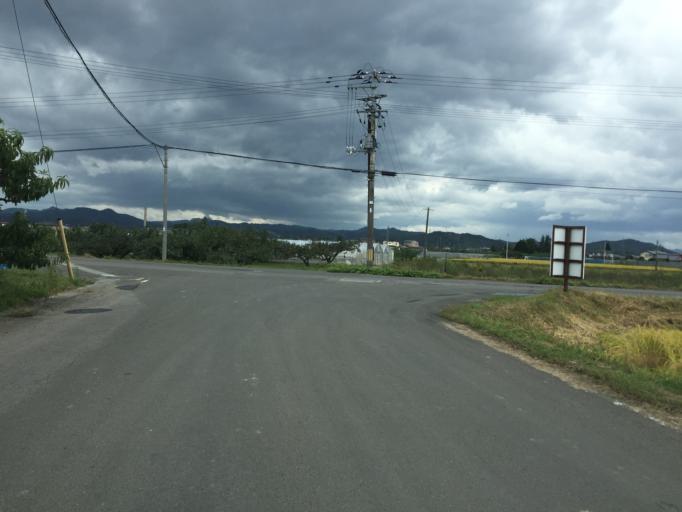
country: JP
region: Fukushima
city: Hobaramachi
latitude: 37.8324
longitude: 140.5484
